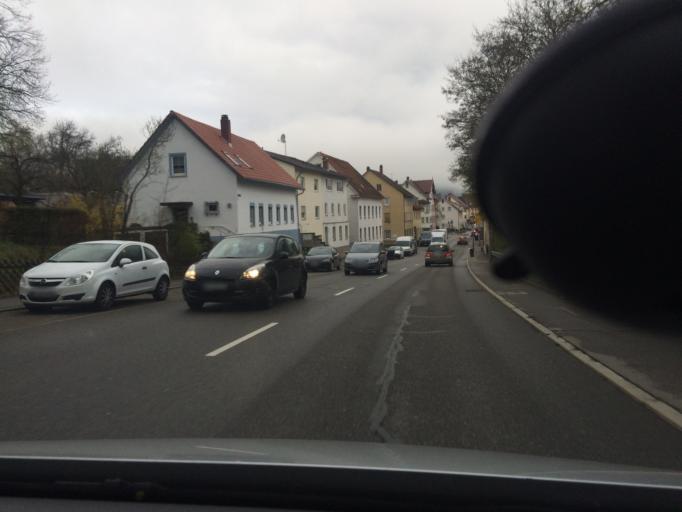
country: DE
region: Baden-Wuerttemberg
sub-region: Freiburg Region
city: Tuttlingen
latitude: 47.9823
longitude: 8.8241
